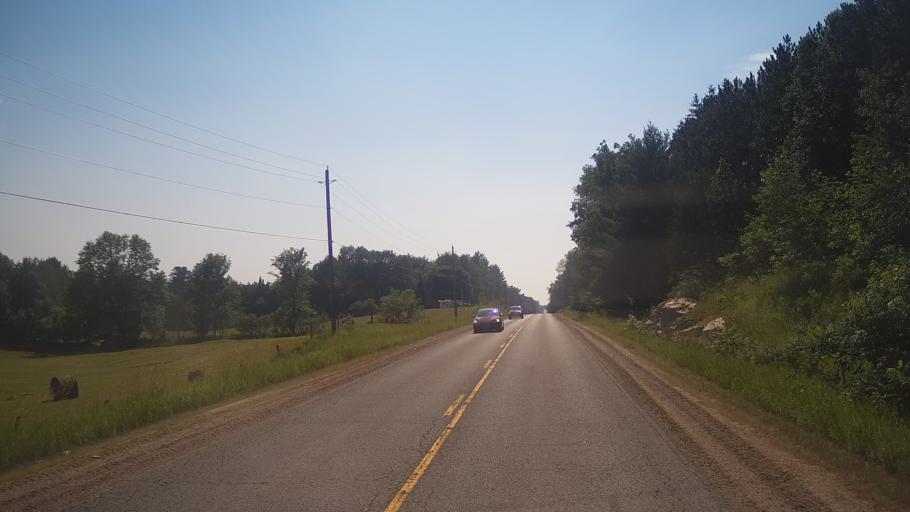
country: CA
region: Ontario
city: Pembroke
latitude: 45.6093
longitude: -77.2071
